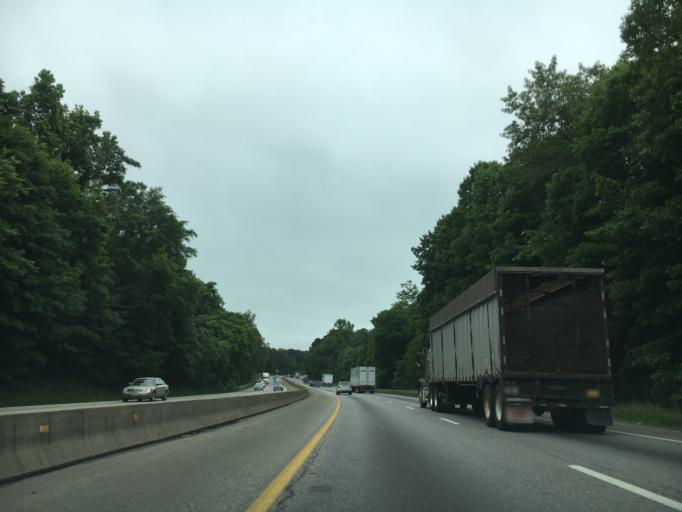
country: US
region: Virginia
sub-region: City of Petersburg
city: Petersburg
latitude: 37.2050
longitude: -77.4126
